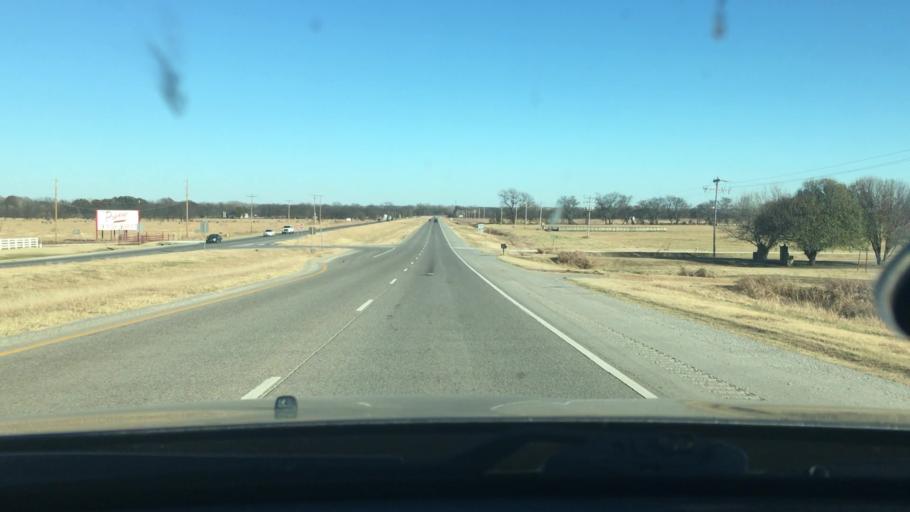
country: US
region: Oklahoma
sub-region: Murray County
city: Davis
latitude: 34.5064
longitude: -97.1702
